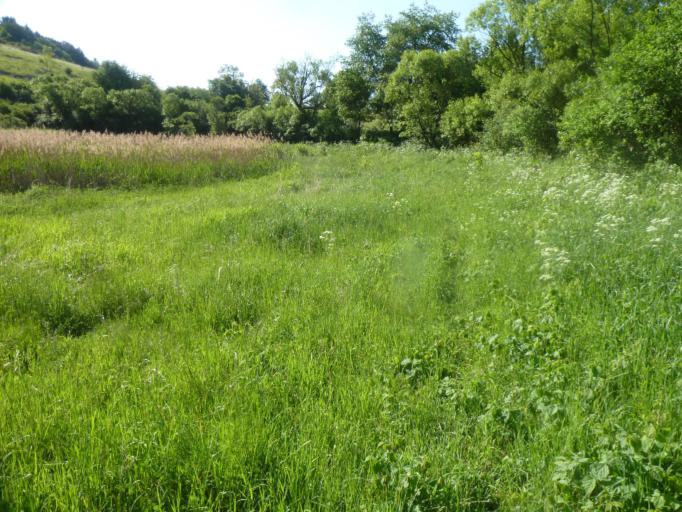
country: HU
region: Borsod-Abauj-Zemplen
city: Rudabanya
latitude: 48.4697
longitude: 20.5103
